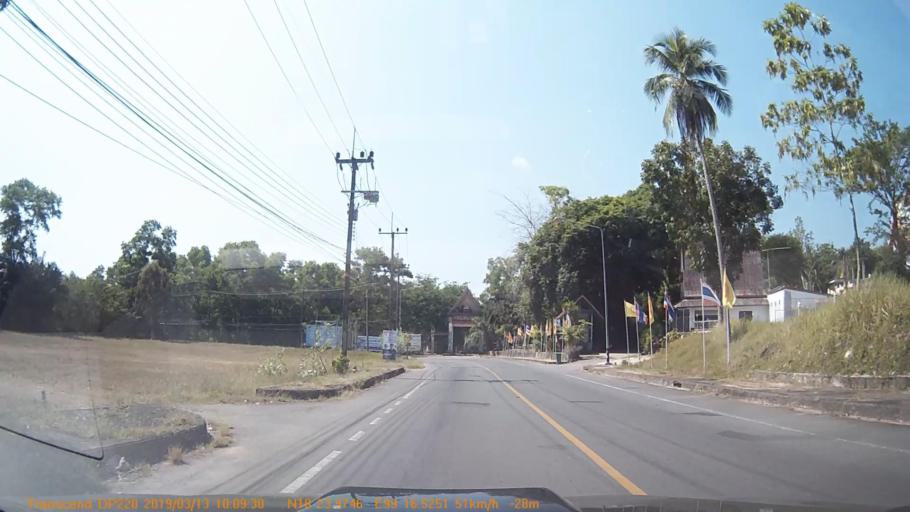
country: TH
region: Chumphon
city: Chumphon
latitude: 10.3999
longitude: 99.2754
